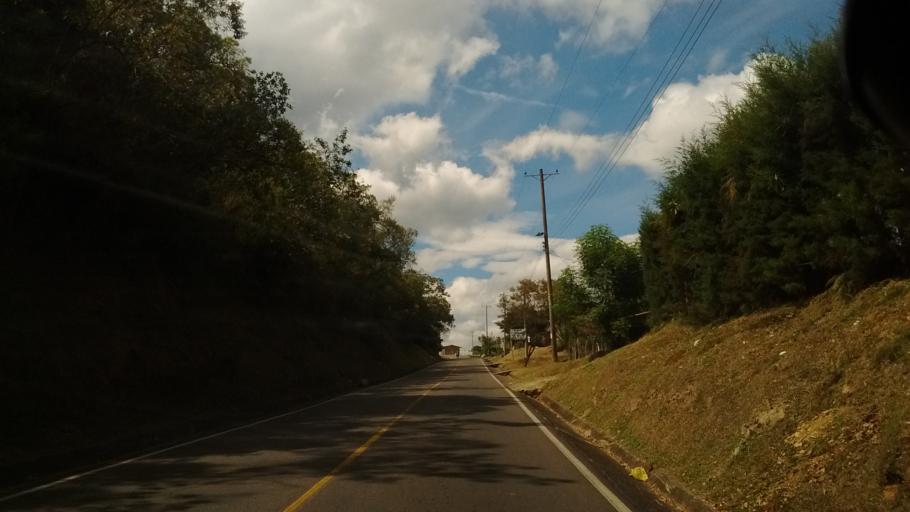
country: CO
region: Cauca
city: Cajibio
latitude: 2.6296
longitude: -76.5142
